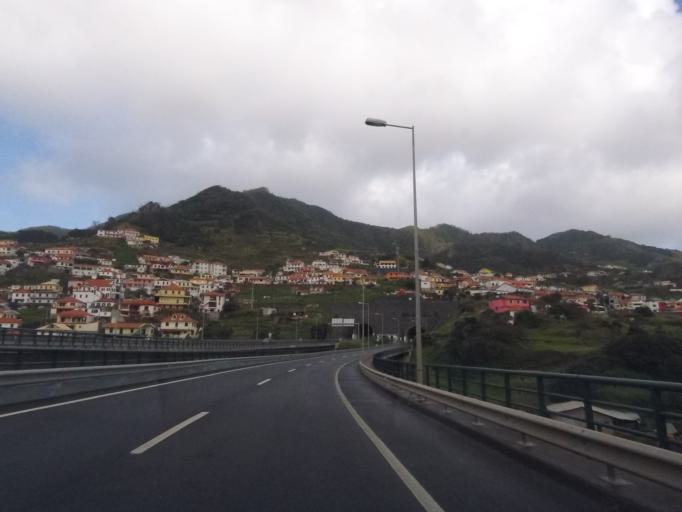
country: PT
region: Madeira
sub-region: Machico
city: Machico
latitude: 32.7316
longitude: -16.7775
